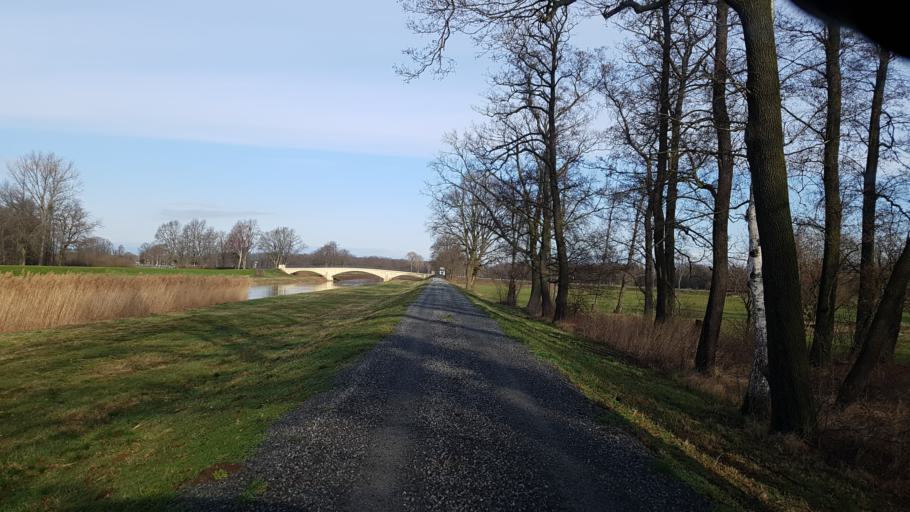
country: DE
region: Brandenburg
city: Falkenberg
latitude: 51.6334
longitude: 13.2793
